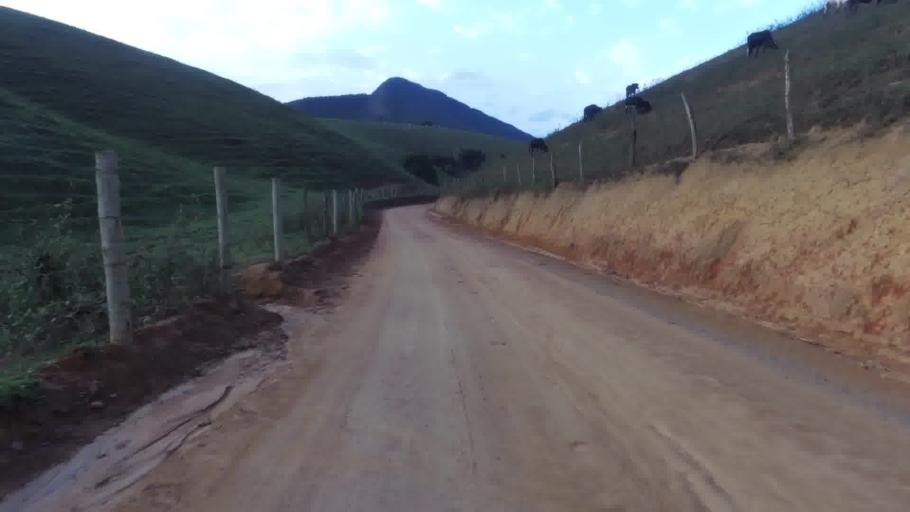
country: BR
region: Espirito Santo
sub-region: Alfredo Chaves
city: Alfredo Chaves
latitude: -20.6927
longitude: -40.6318
